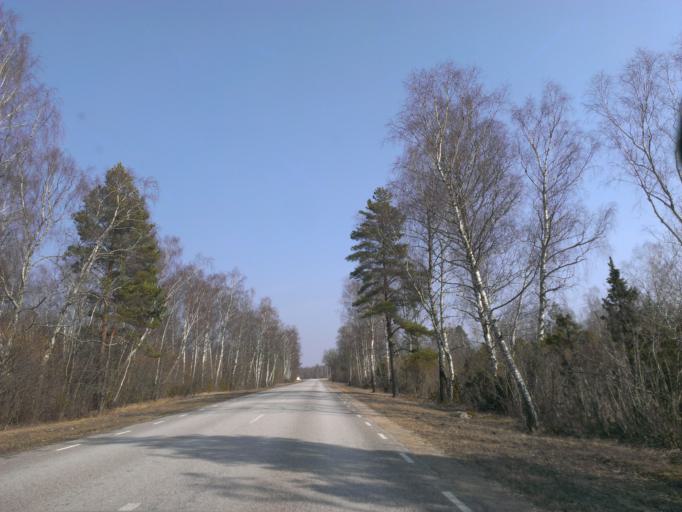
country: EE
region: Saare
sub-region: Kuressaare linn
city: Kuressaare
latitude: 58.2715
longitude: 22.6157
